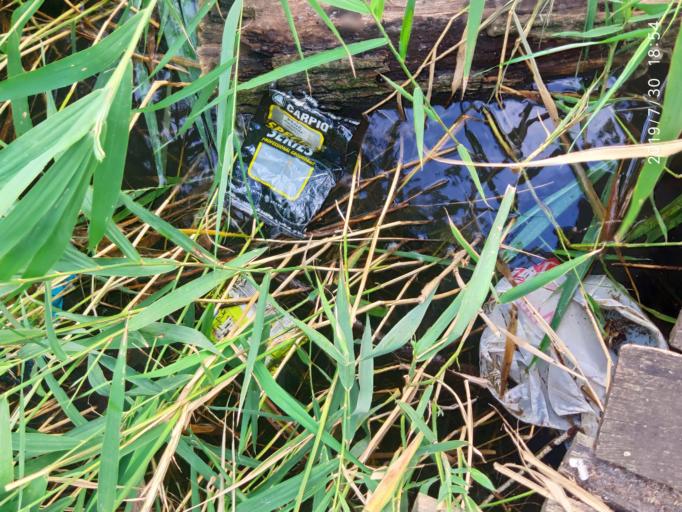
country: PL
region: Lubusz
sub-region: Powiat swiebodzinski
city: Miedzylesie
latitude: 52.1658
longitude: 15.2835
